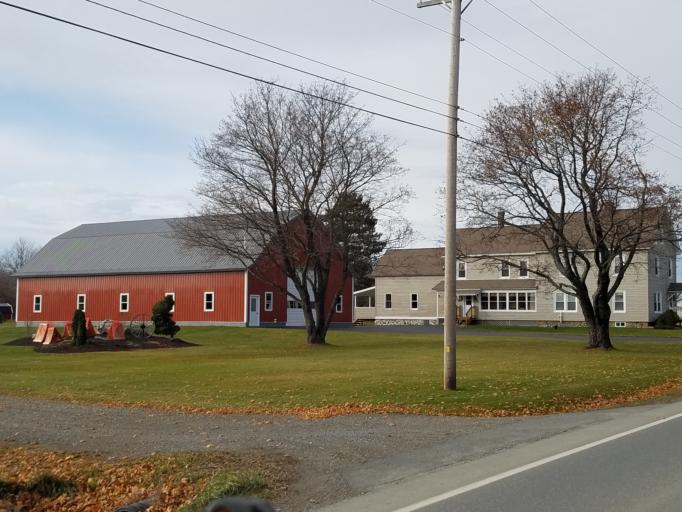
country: US
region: Maine
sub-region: Aroostook County
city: Presque Isle
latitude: 46.6130
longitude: -68.3994
